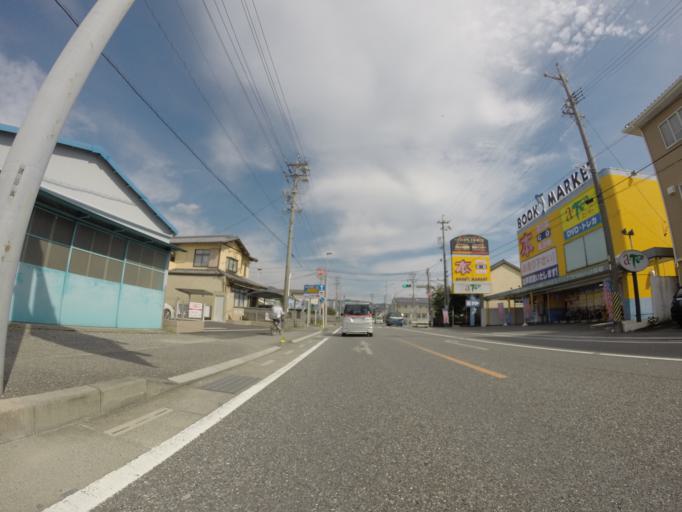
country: JP
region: Shizuoka
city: Shizuoka-shi
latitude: 35.0352
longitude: 138.4926
